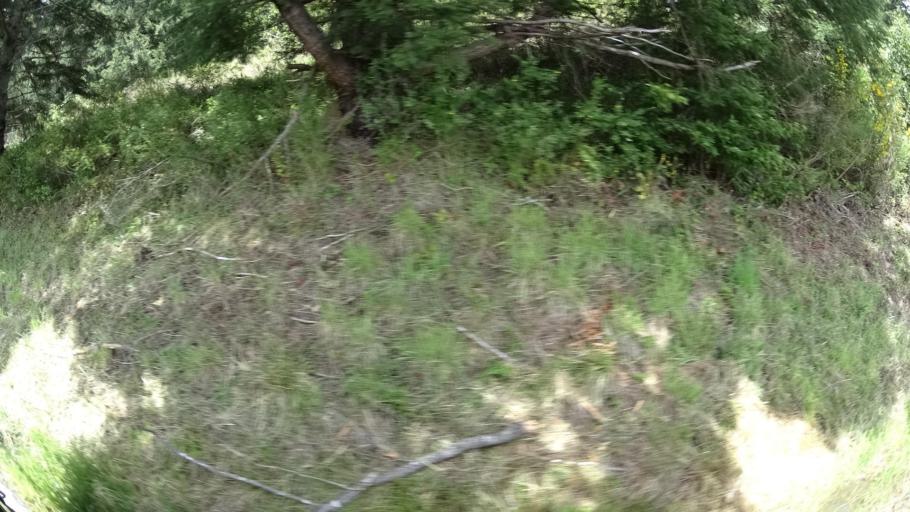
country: US
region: California
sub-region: Humboldt County
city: Blue Lake
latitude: 40.7661
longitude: -123.9446
